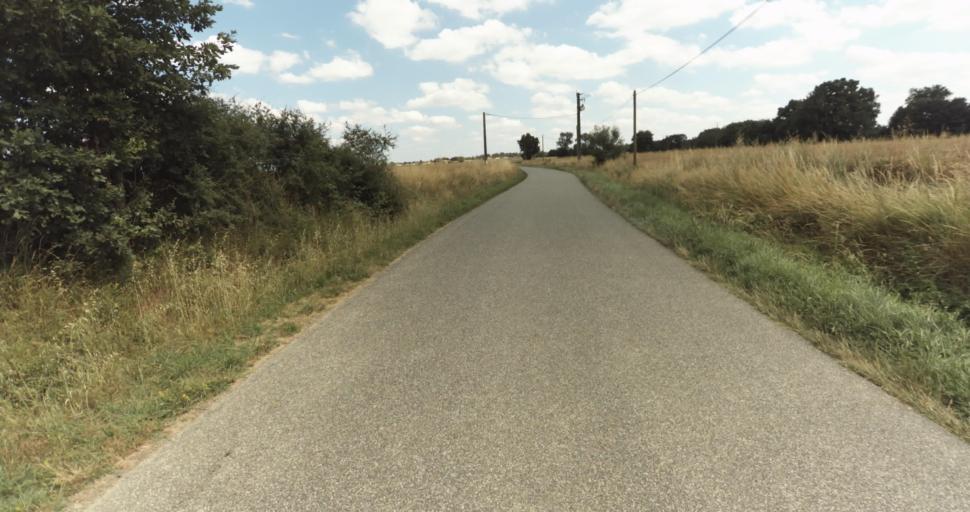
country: FR
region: Midi-Pyrenees
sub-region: Departement de la Haute-Garonne
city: Fontenilles
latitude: 43.5619
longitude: 1.1788
